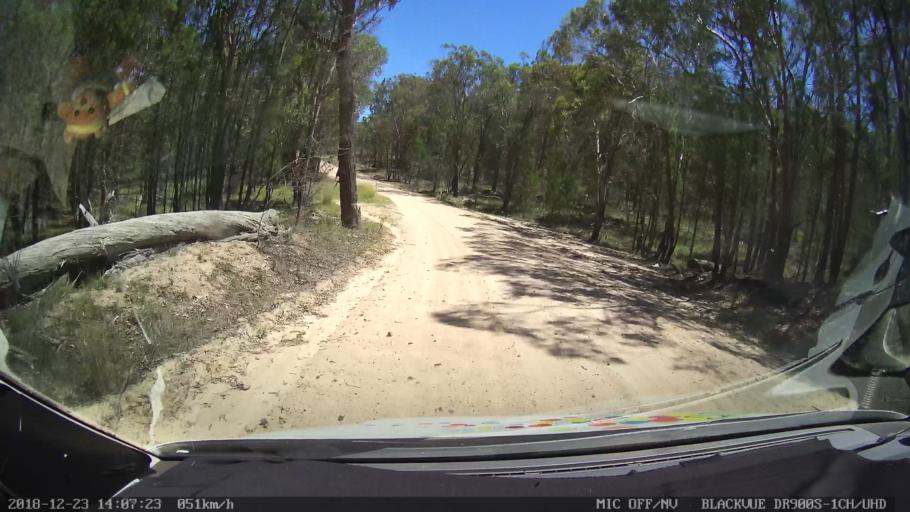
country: AU
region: New South Wales
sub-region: Tamworth Municipality
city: Manilla
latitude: -30.6355
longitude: 151.0718
